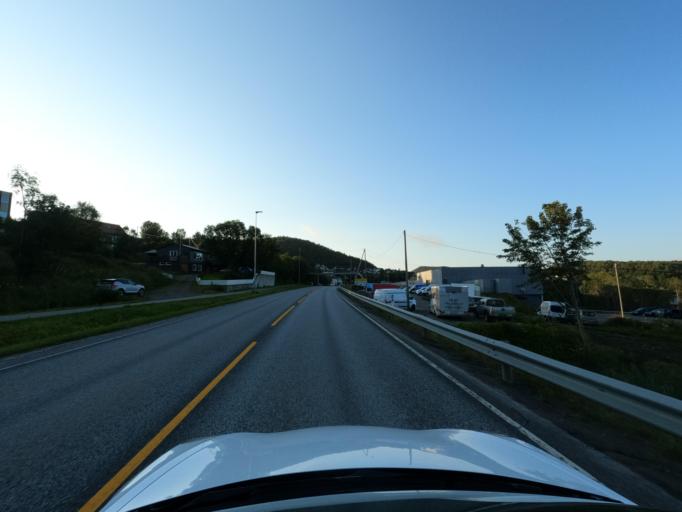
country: NO
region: Troms
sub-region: Harstad
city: Harstad
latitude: 68.7697
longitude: 16.5580
